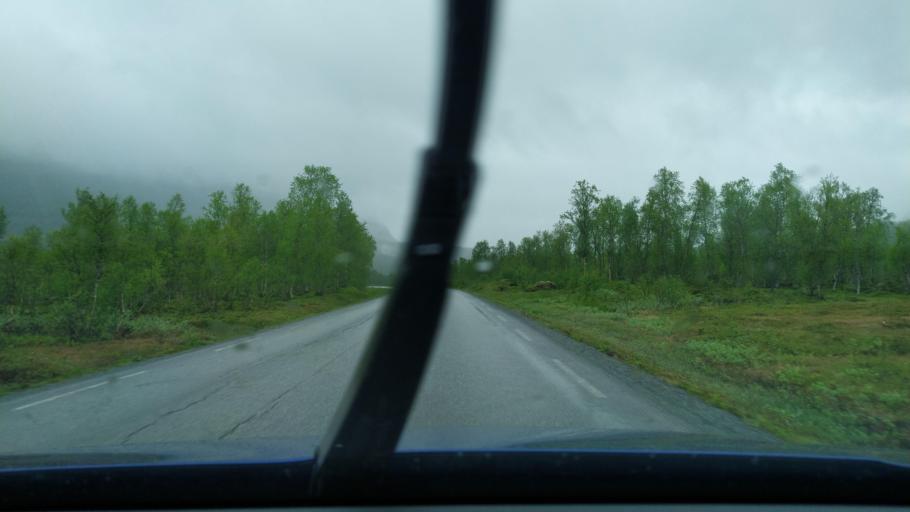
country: NO
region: Troms
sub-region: Dyroy
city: Brostadbotn
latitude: 69.0292
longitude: 17.7382
